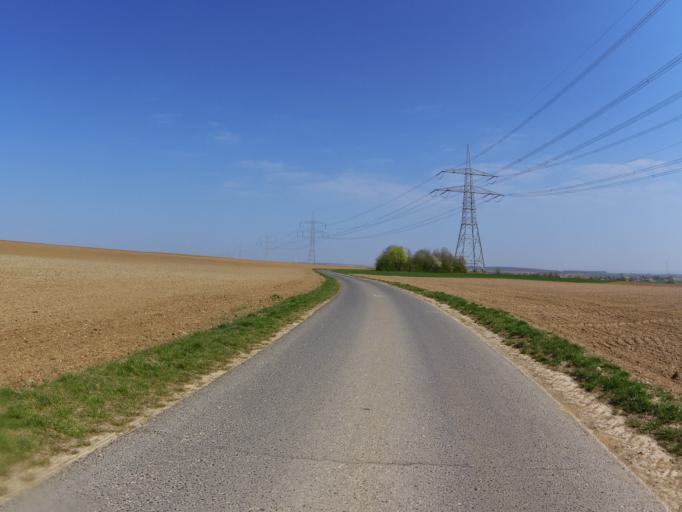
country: DE
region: Bavaria
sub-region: Regierungsbezirk Unterfranken
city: Biebelried
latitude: 49.8139
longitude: 10.0801
